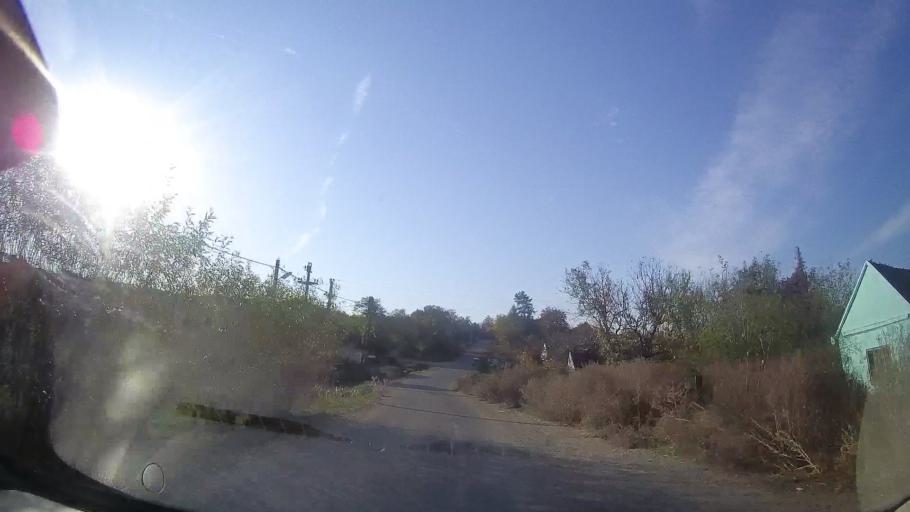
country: RO
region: Timis
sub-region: Comuna Bogda
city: Bogda
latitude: 45.9594
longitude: 21.6145
